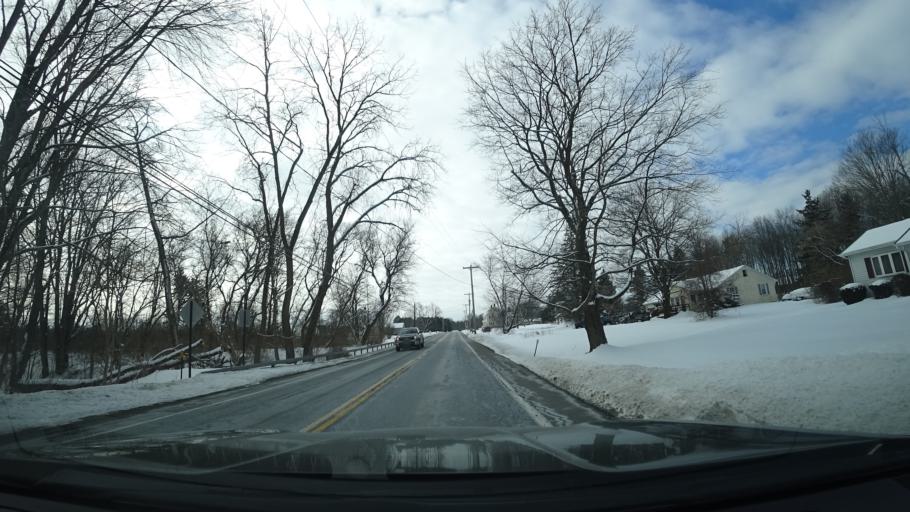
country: US
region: New York
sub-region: Washington County
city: Fort Edward
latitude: 43.2679
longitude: -73.6087
